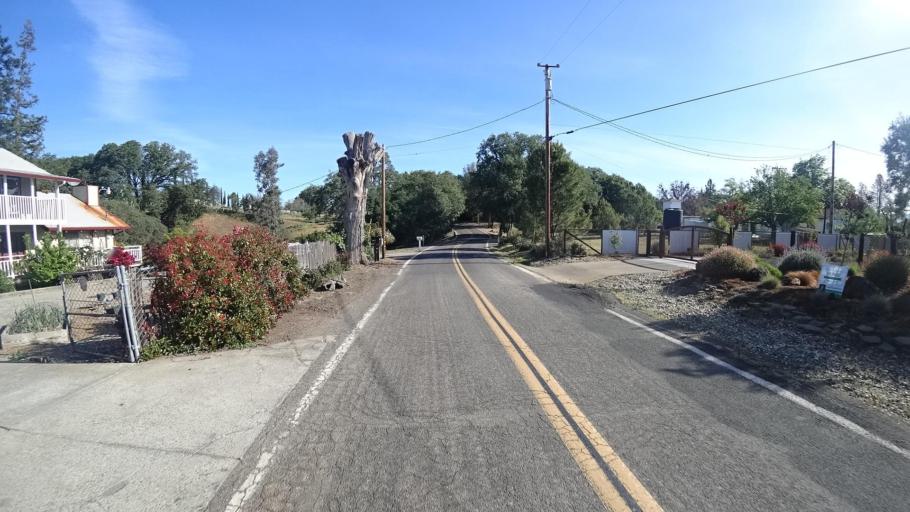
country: US
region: California
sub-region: Lake County
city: Lakeport
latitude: 39.0422
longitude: -122.9508
